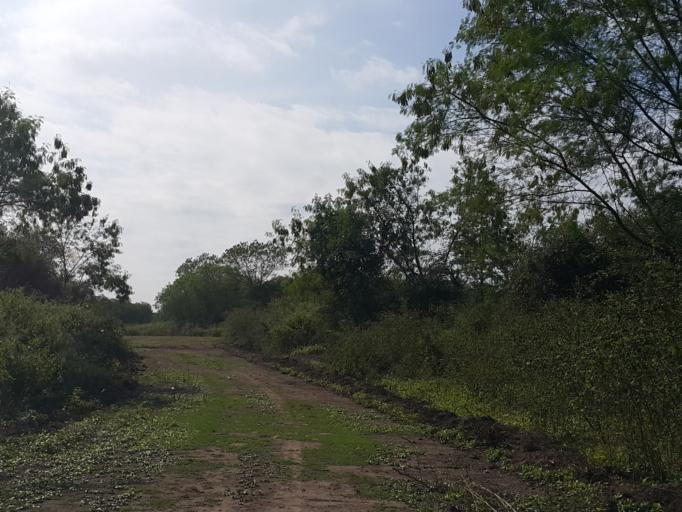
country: TH
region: Lampang
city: Mae Mo
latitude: 18.3393
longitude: 99.7641
